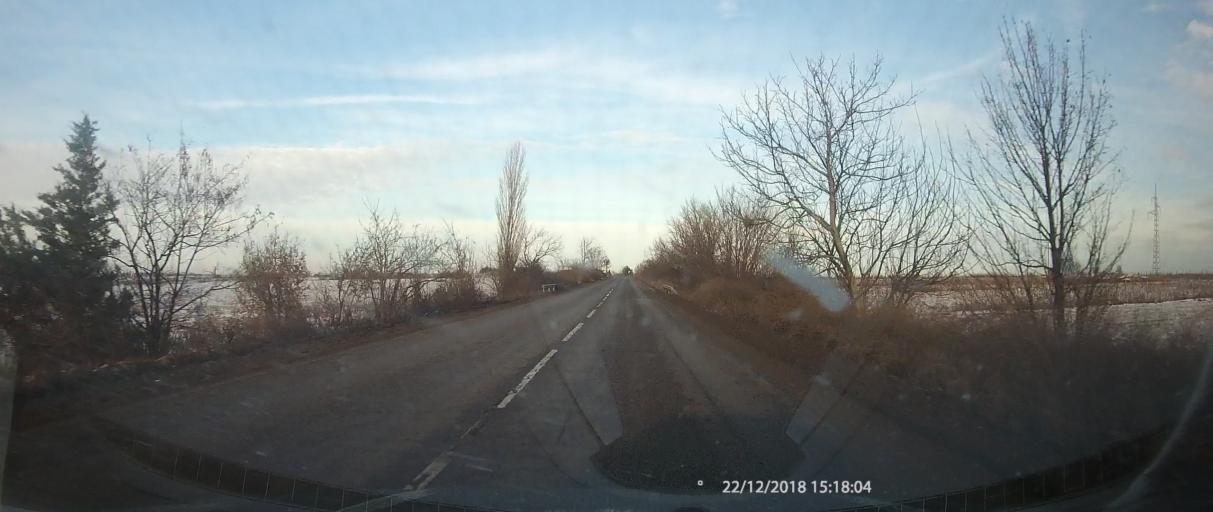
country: BG
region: Ruse
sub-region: Obshtina Dve Mogili
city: Dve Mogili
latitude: 43.6347
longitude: 25.8685
